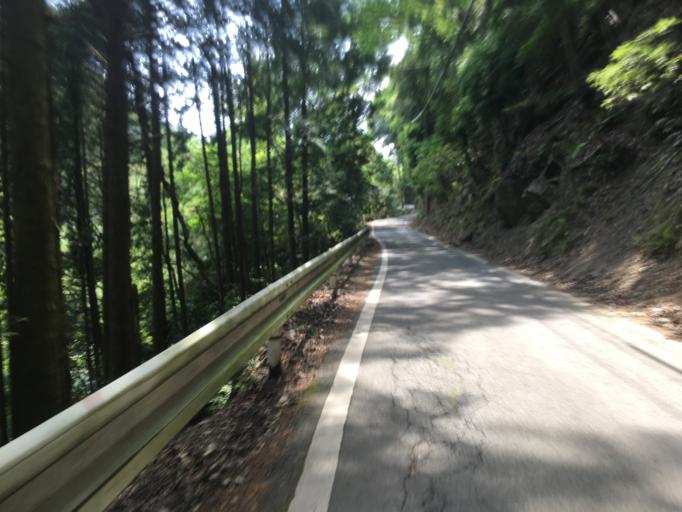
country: JP
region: Kyoto
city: Kameoka
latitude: 35.0259
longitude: 135.6447
